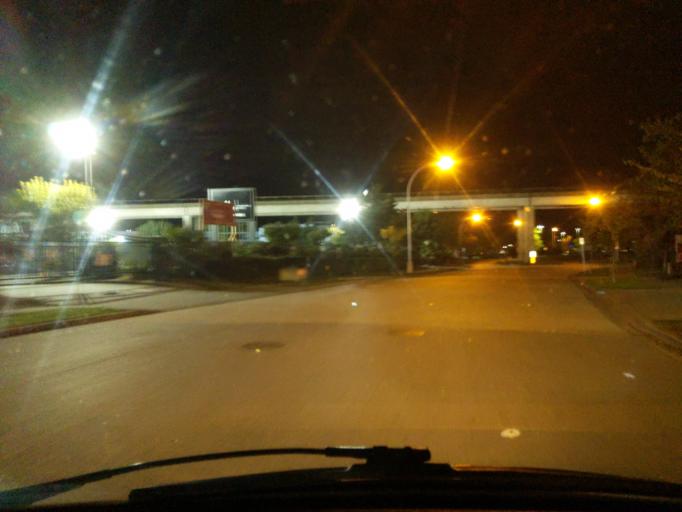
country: CA
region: British Columbia
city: New Westminster
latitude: 49.2029
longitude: -122.8801
